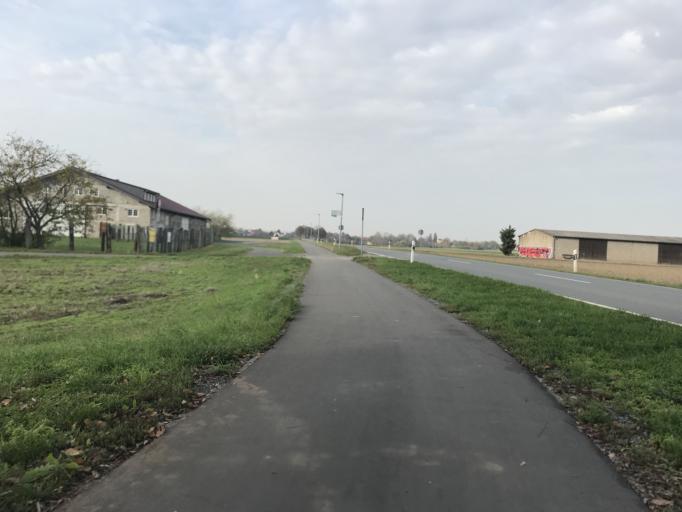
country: DE
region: Hesse
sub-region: Regierungsbezirk Darmstadt
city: Trebur
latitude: 49.9301
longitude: 8.3953
